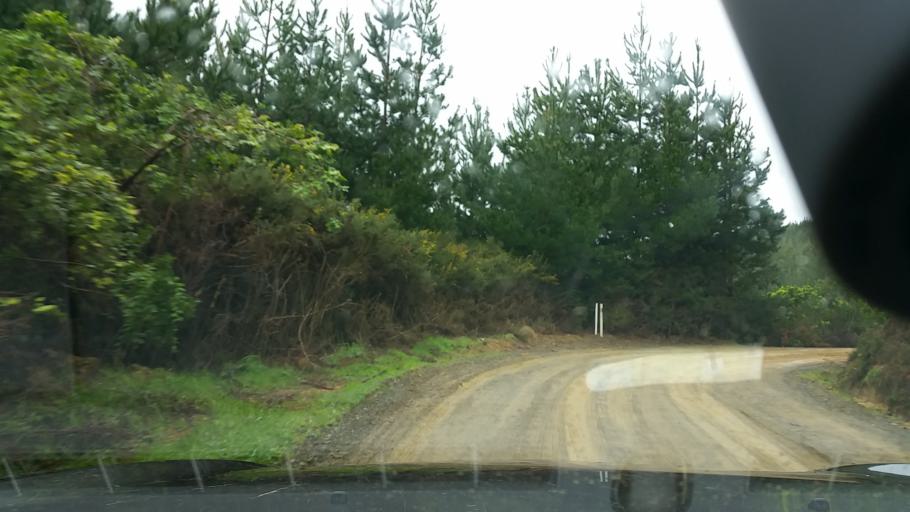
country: NZ
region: Marlborough
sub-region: Marlborough District
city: Picton
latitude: -41.3628
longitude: 174.0718
